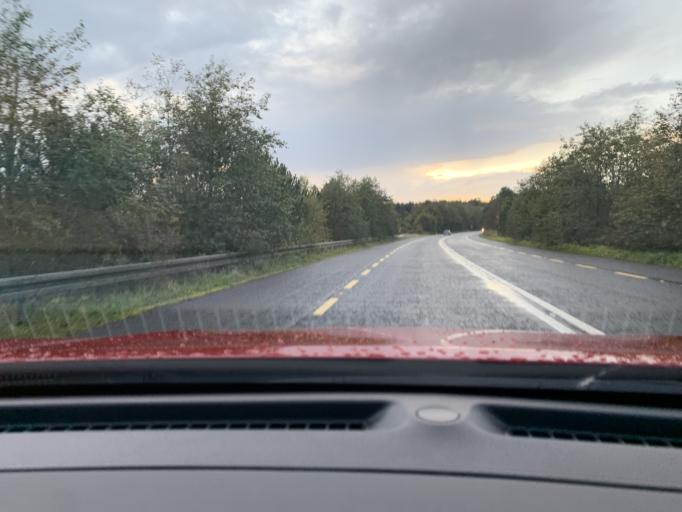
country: IE
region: Connaught
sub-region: County Leitrim
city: Carrick-on-Shannon
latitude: 53.9485
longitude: -8.1395
